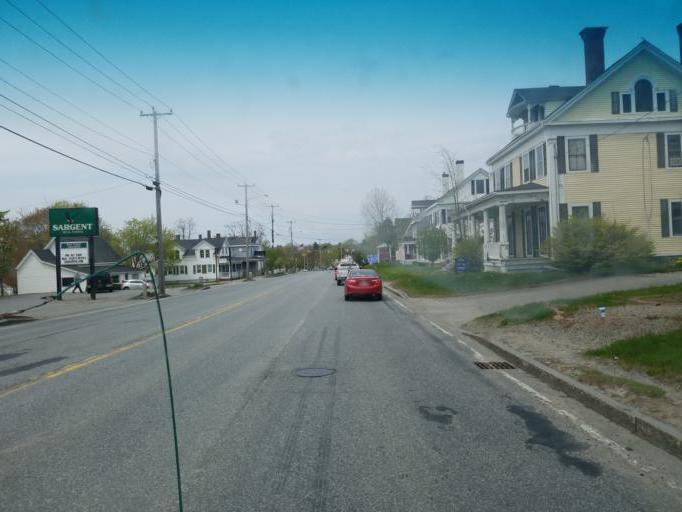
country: US
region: Maine
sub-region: Hancock County
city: Ellsworth
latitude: 44.5417
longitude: -68.4186
